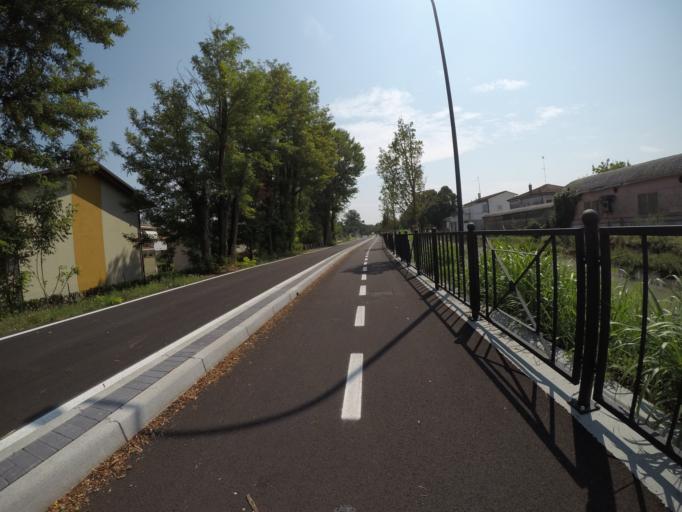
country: IT
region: Veneto
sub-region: Provincia di Rovigo
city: Lendinara
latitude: 45.0852
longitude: 11.5917
